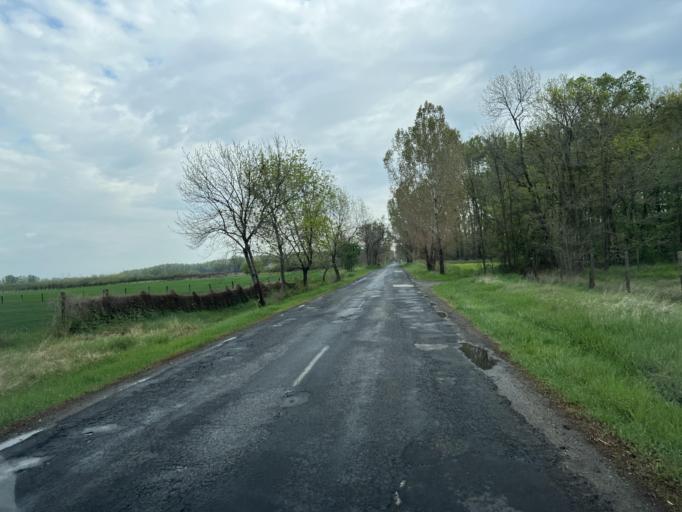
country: HU
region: Pest
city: Danszentmiklos
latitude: 47.2117
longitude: 19.5693
